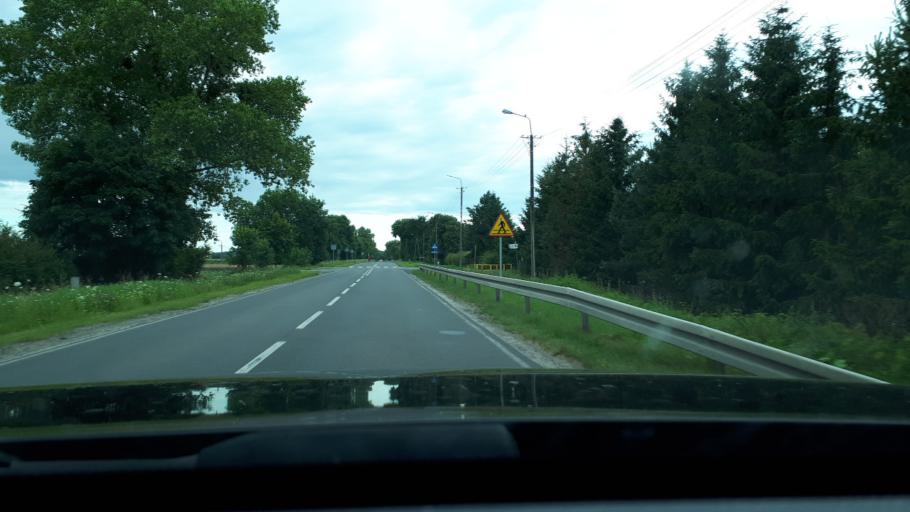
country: PL
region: Warmian-Masurian Voivodeship
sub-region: Powiat olsztynski
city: Olsztynek
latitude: 53.5754
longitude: 20.2755
